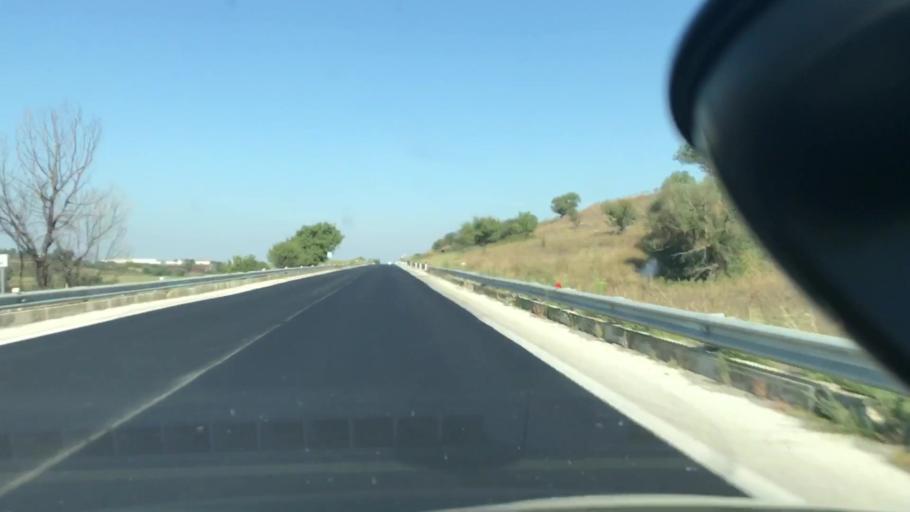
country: IT
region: Apulia
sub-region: Provincia di Barletta - Andria - Trani
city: Spinazzola
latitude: 40.9041
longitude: 16.1149
